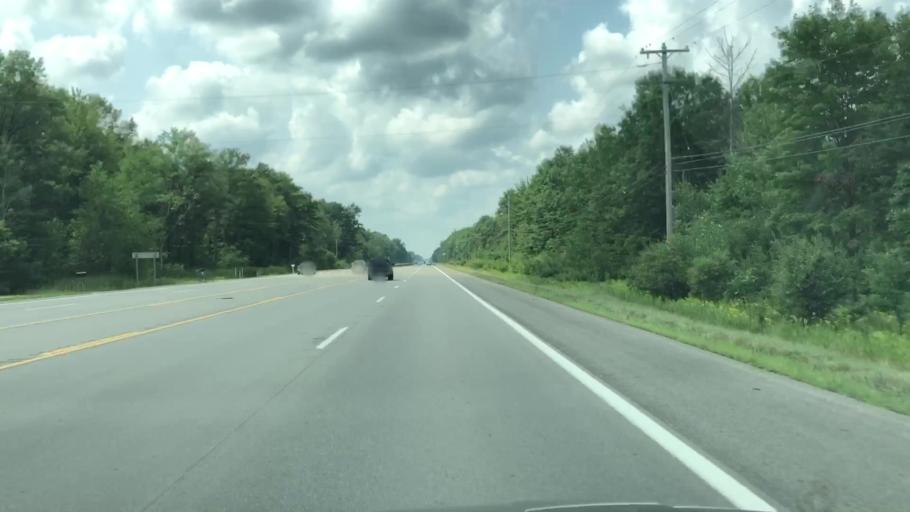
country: US
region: Michigan
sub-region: Midland County
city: Coleman
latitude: 43.6115
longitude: -84.4907
